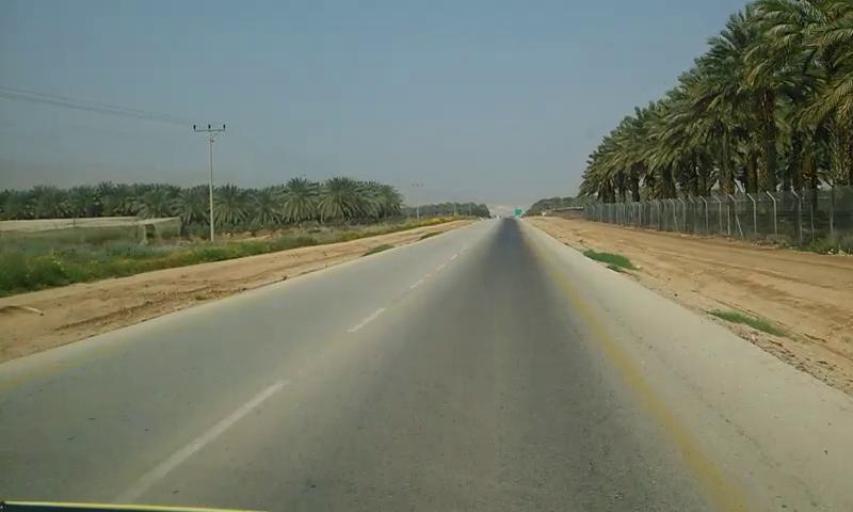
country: PS
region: West Bank
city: Al Fasayil
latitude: 31.9945
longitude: 35.4572
